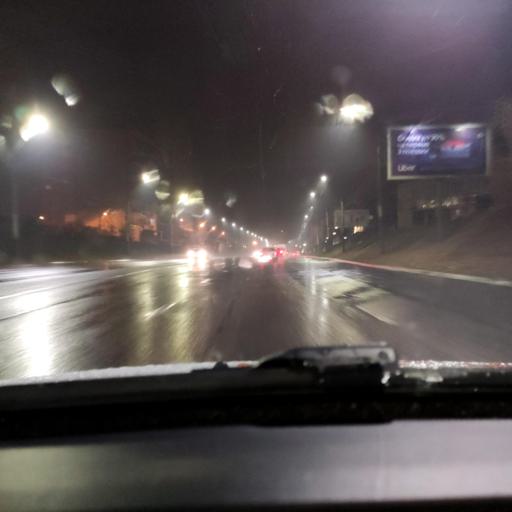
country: RU
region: Voronezj
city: Voronezh
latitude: 51.6430
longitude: 39.2019
